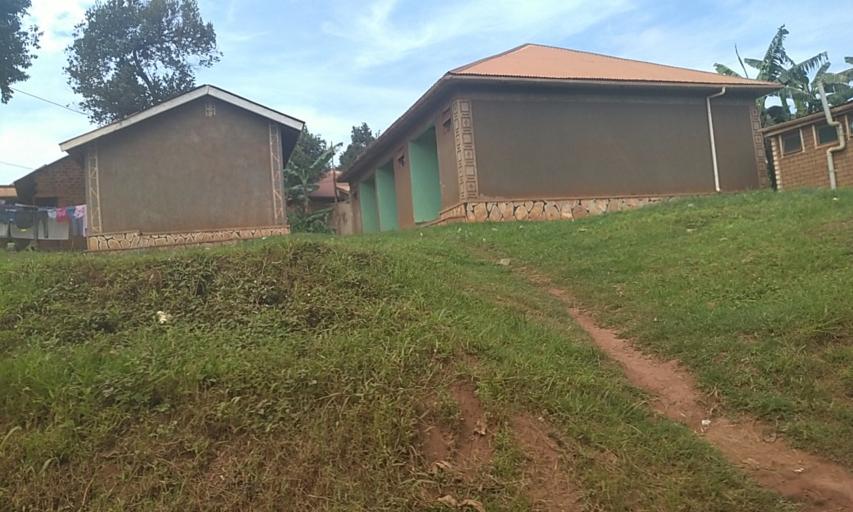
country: UG
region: Central Region
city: Kampala Central Division
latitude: 0.2834
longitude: 32.5175
